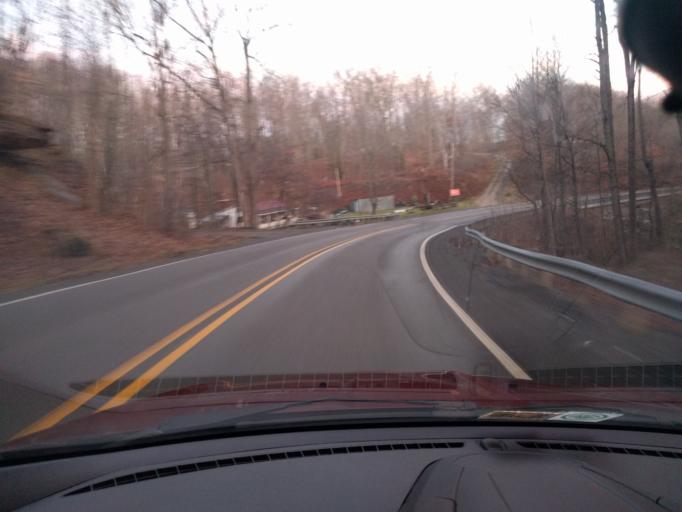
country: US
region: West Virginia
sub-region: Greenbrier County
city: Rainelle
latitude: 38.0232
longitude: -80.9166
